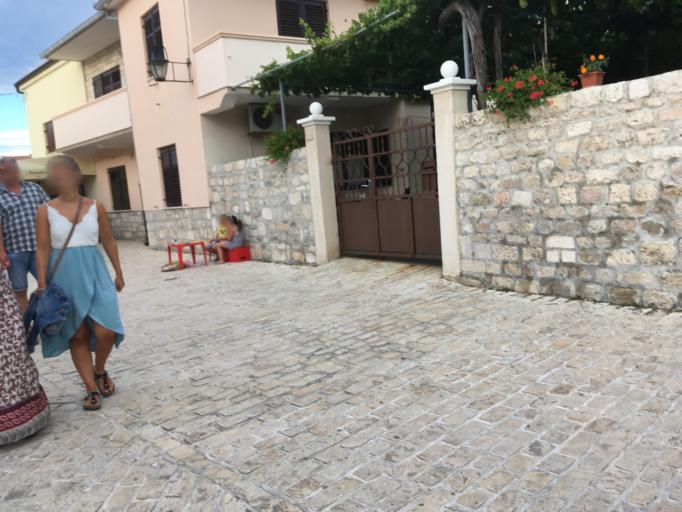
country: HR
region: Zadarska
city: Nin
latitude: 44.2430
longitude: 15.1839
